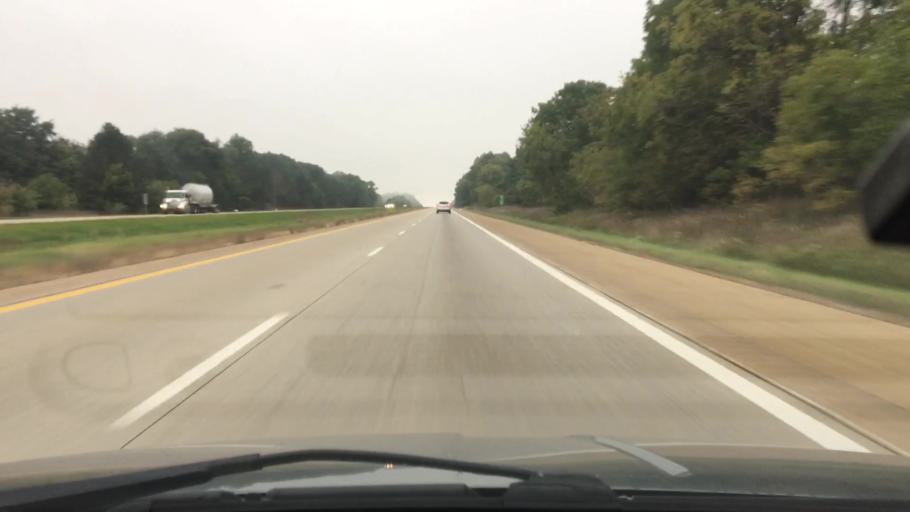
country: US
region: Michigan
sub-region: Jackson County
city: Concord
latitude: 42.2622
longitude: -84.6648
